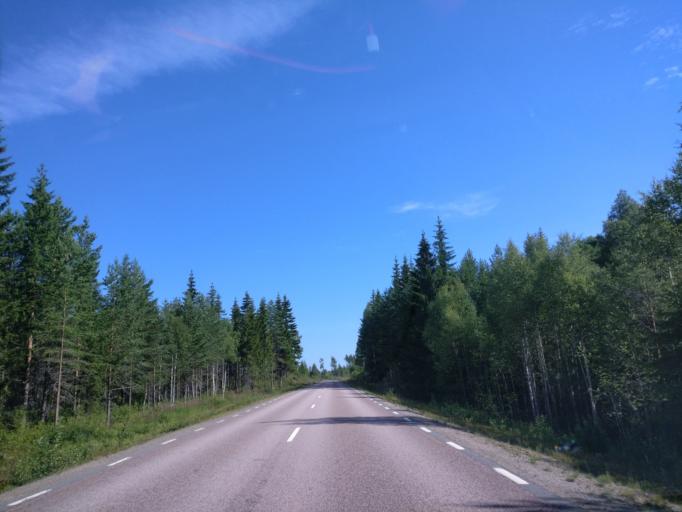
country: SE
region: Vaermland
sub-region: Hagfors Kommun
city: Hagfors
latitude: 60.0345
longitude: 13.9194
